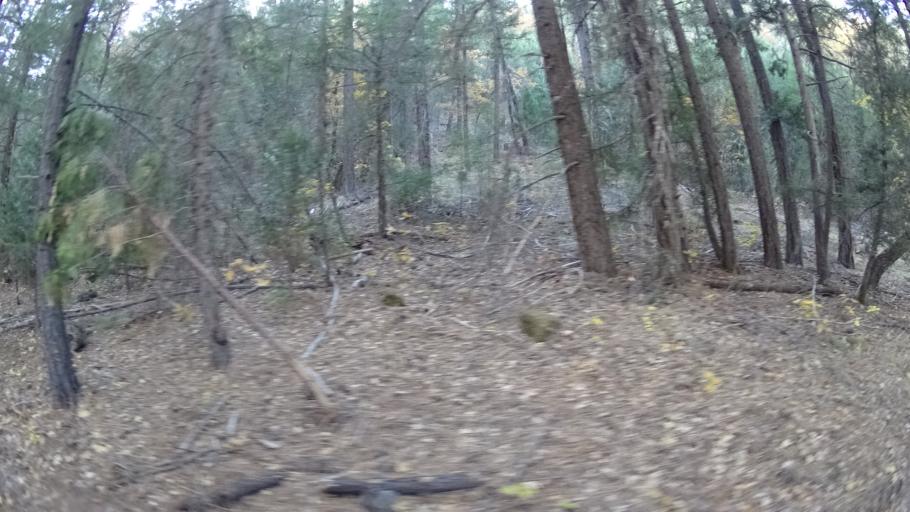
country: US
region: California
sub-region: Siskiyou County
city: Yreka
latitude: 41.8640
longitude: -122.7950
